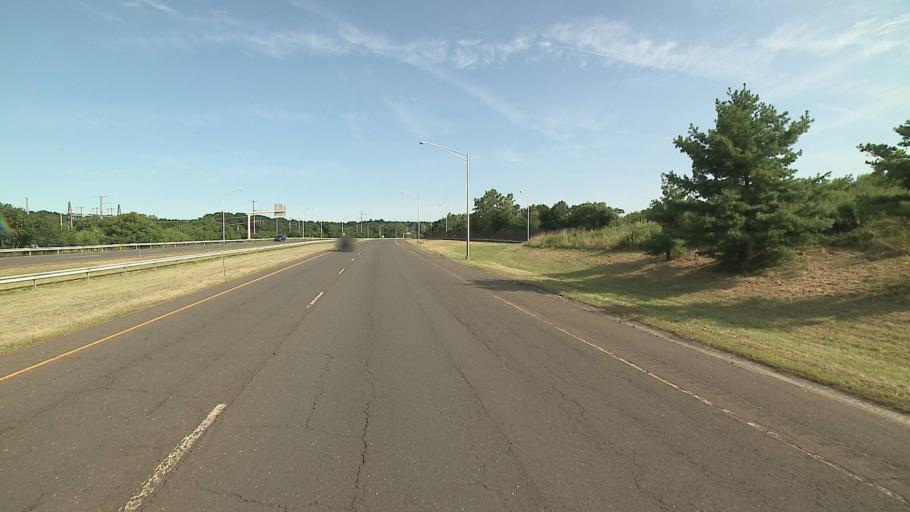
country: US
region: Connecticut
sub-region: Fairfield County
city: Norwalk
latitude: 41.1277
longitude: -73.4271
